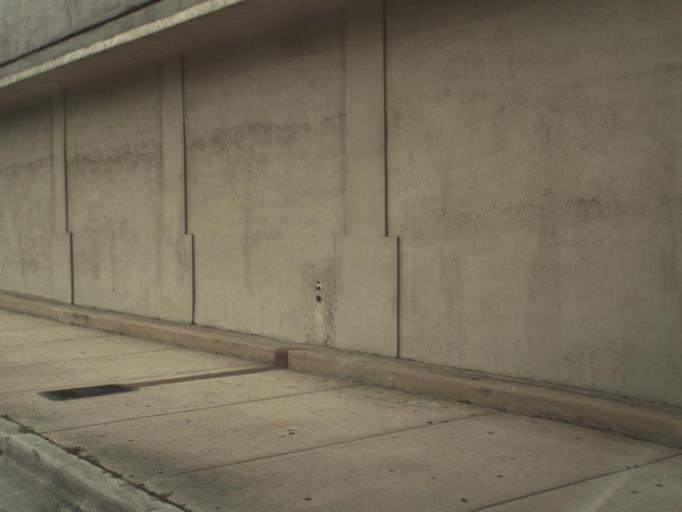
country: US
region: Florida
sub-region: Miami-Dade County
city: West Miami
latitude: 25.7640
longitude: -80.2790
